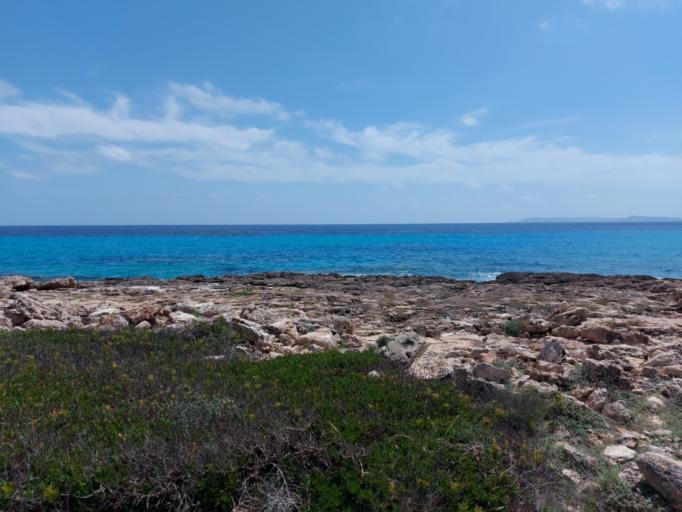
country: ES
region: Balearic Islands
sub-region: Illes Balears
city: Ses Salines
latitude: 39.2649
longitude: 3.0552
